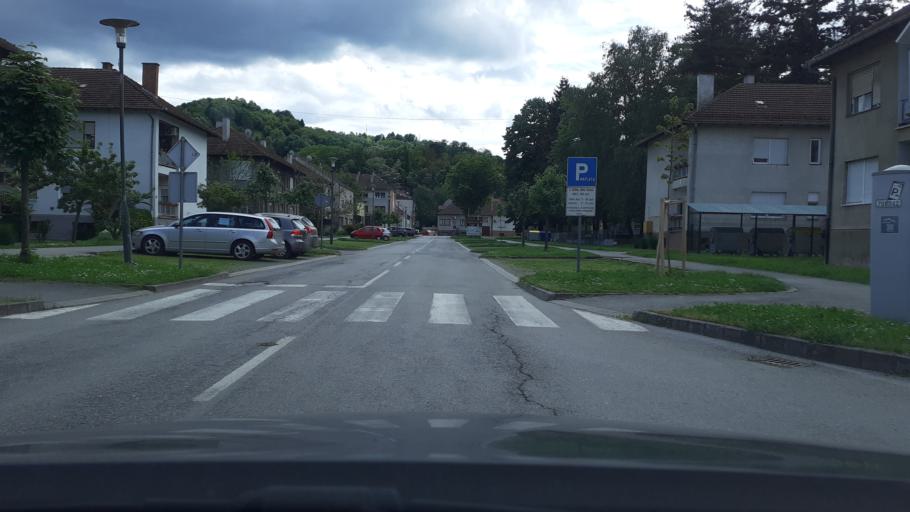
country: HR
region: Pozesko-Slavonska
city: Pozega
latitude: 45.3360
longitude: 17.6812
